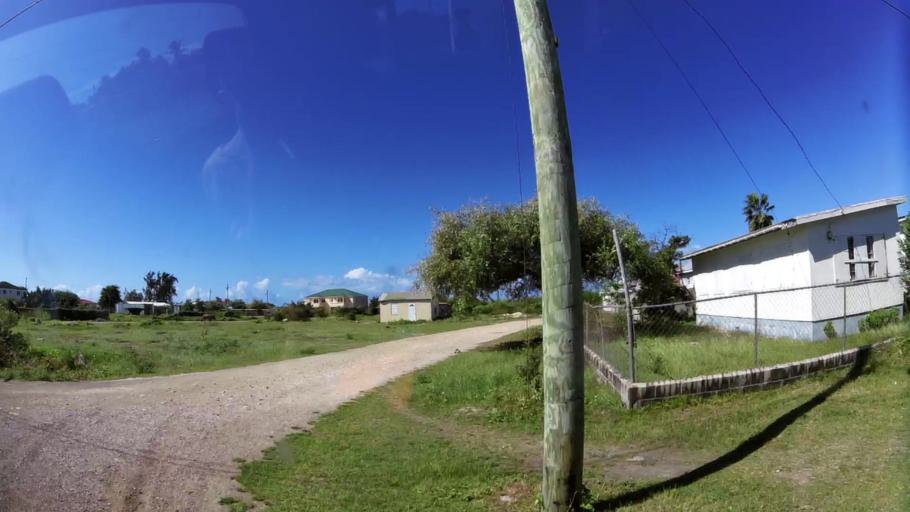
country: AG
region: Barbuda
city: Codrington
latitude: 17.6427
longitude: -61.8256
